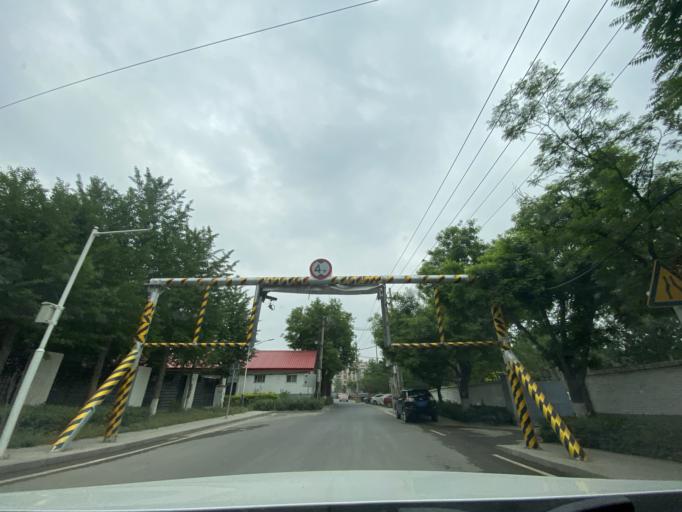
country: CN
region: Beijing
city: Sijiqing
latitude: 39.9339
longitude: 116.2389
